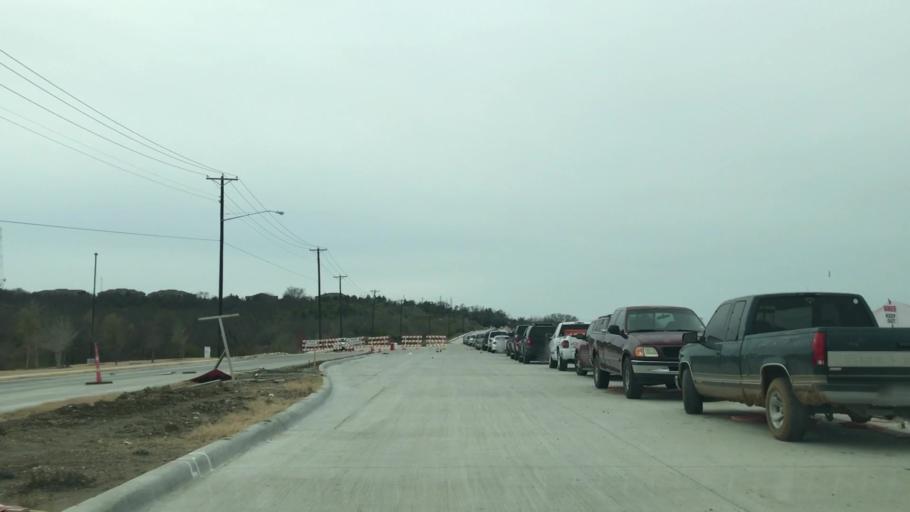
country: US
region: Texas
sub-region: Dallas County
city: Cockrell Hill
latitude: 32.7556
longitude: -96.9022
